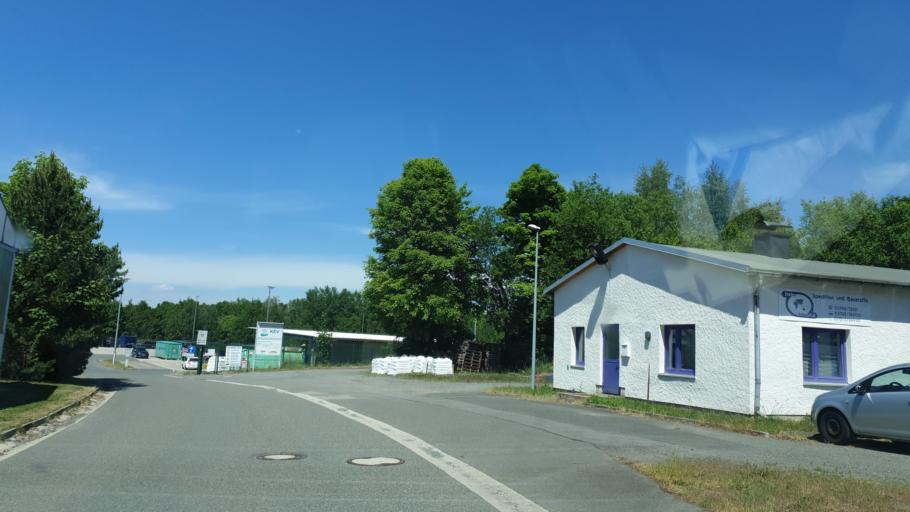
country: DE
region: Saxony
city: Neustadt Vogtland
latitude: 50.4741
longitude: 12.3485
